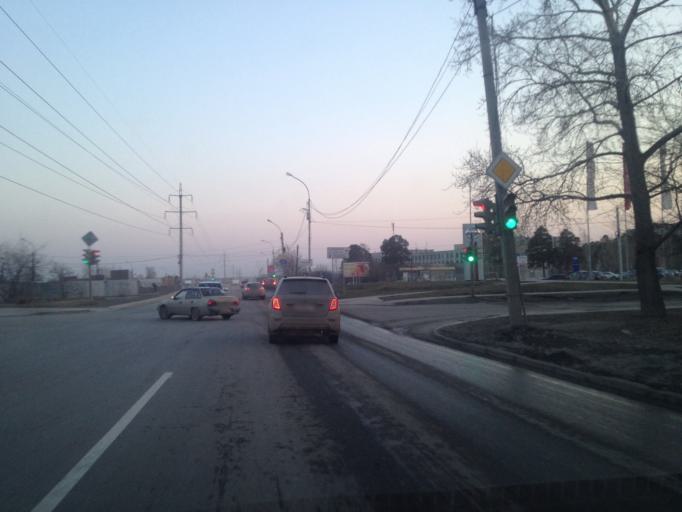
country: RU
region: Sverdlovsk
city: Sovkhoznyy
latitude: 56.7658
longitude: 60.5929
